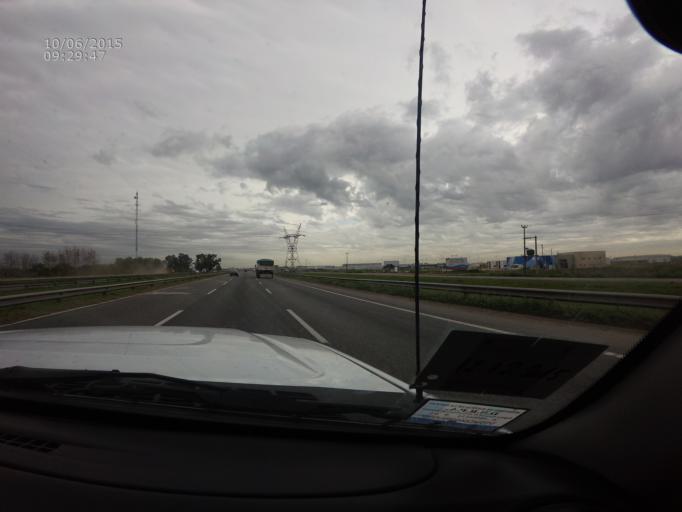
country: AR
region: Buenos Aires
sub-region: Partido de Zarate
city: Zarate
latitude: -34.1463
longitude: -59.0336
